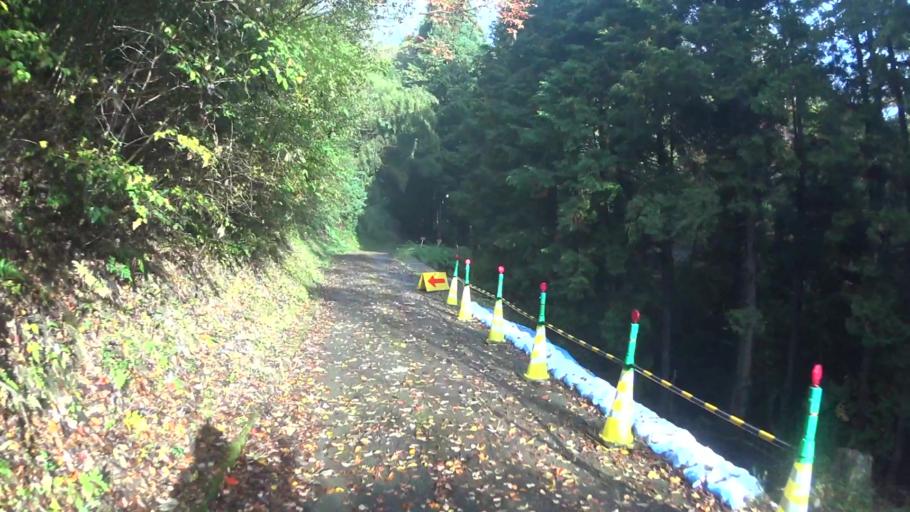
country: JP
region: Kyoto
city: Ayabe
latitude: 35.2653
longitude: 135.2256
